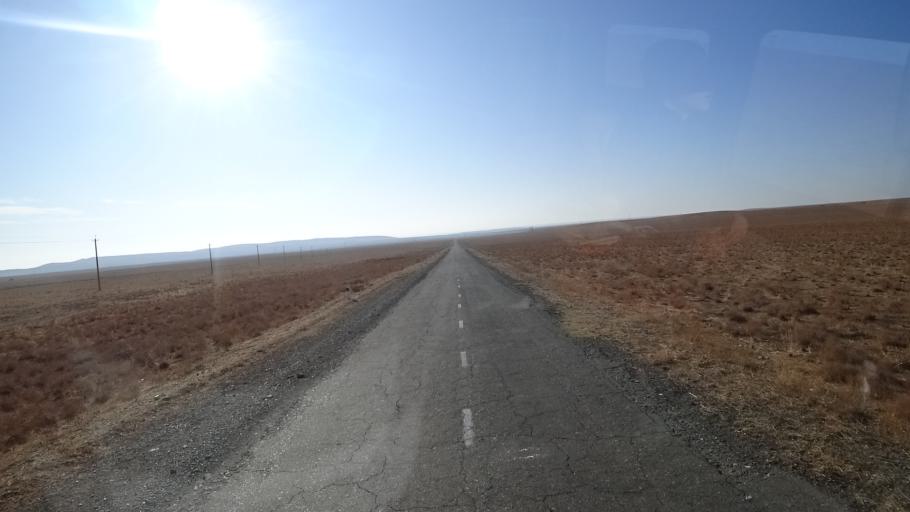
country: UZ
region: Navoiy
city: Karmana Shahri
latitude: 40.2725
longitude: 65.5350
